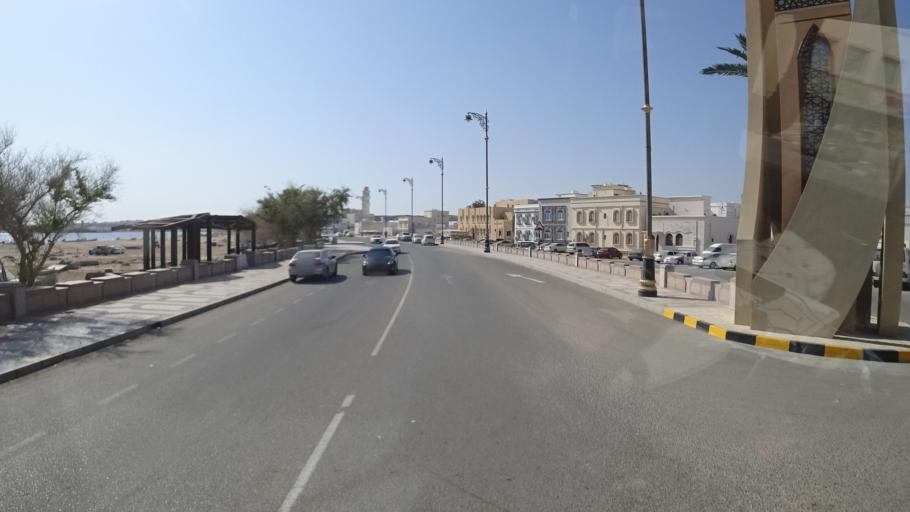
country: OM
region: Ash Sharqiyah
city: Sur
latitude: 22.5722
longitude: 59.5283
